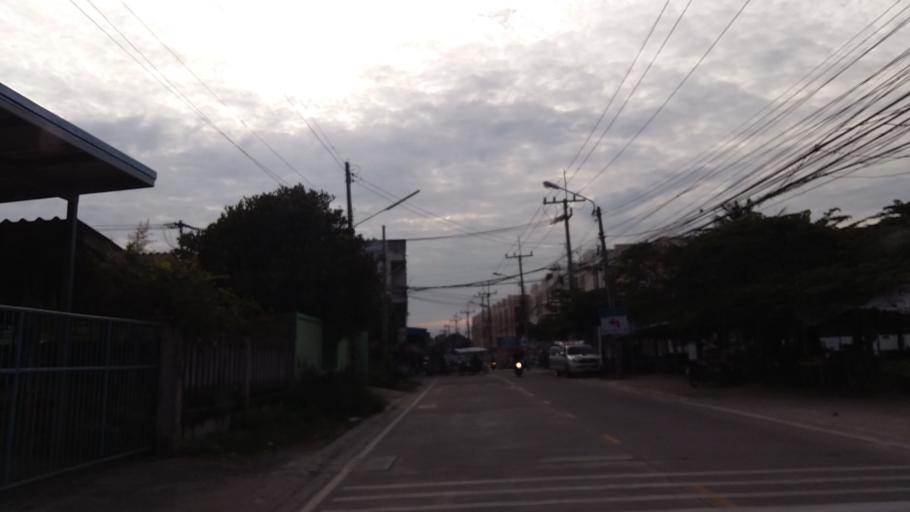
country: TH
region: Chon Buri
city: Chon Buri
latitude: 13.3158
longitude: 100.9377
